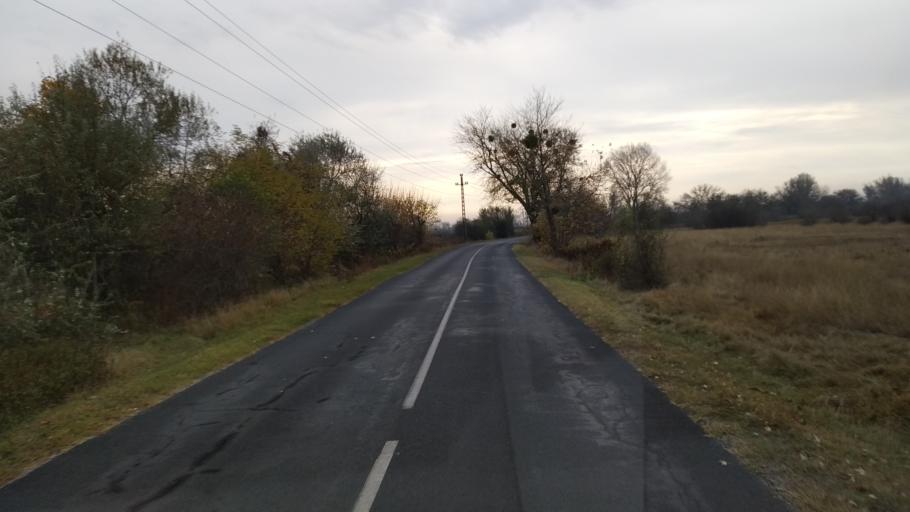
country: HU
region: Pest
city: Tahitotfalu
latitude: 47.7834
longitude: 19.0925
